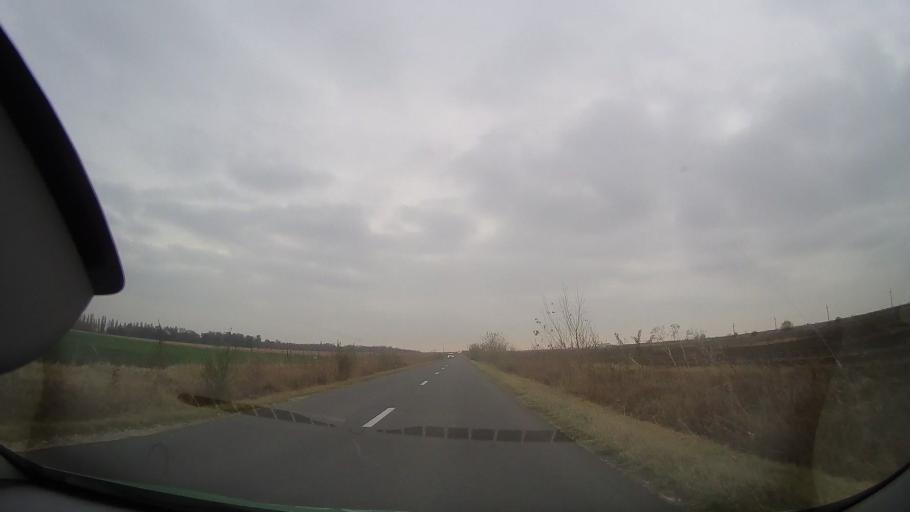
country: RO
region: Ialomita
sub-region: Comuna Alexeni
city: Alexeni
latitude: 44.7396
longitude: 26.7081
